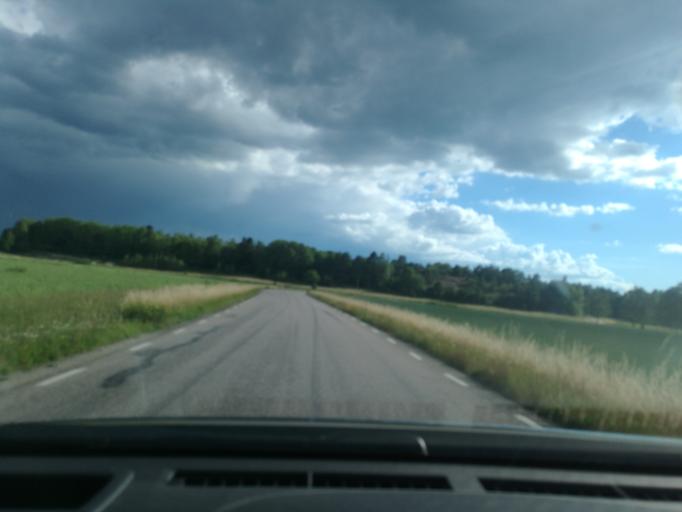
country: SE
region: Soedermanland
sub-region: Eskilstuna Kommun
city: Arla
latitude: 59.4165
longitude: 16.7048
